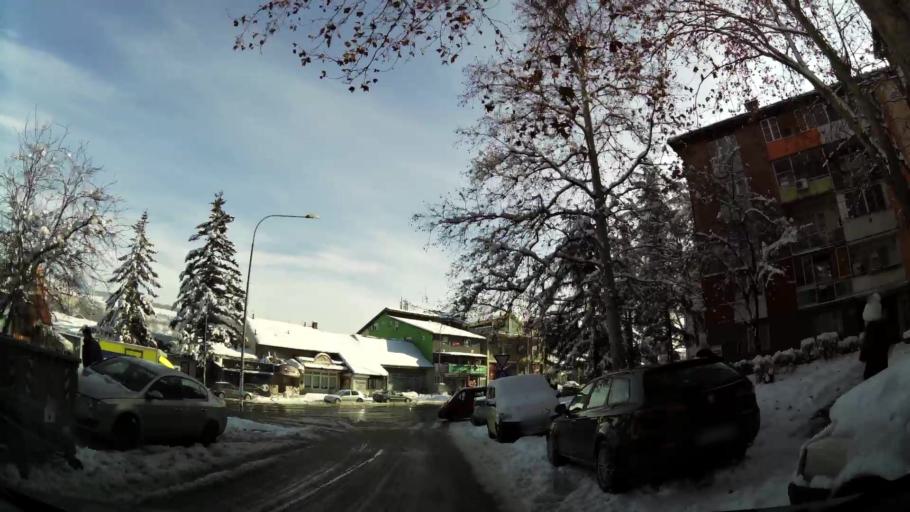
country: RS
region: Central Serbia
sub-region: Belgrade
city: Palilula
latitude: 44.8054
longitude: 20.5245
